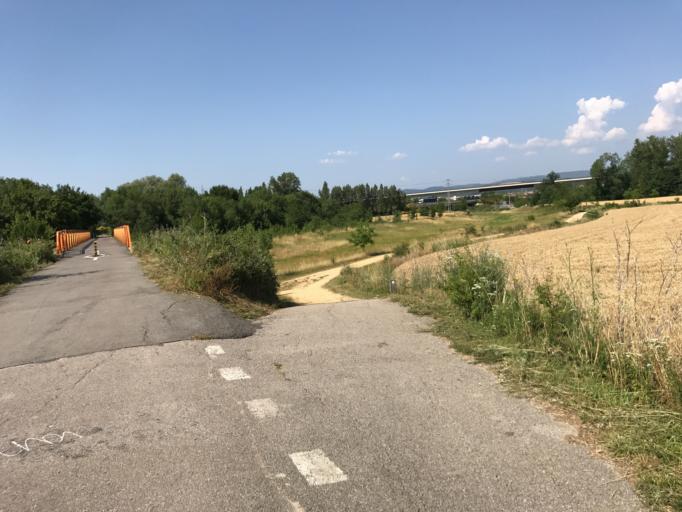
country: ES
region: Basque Country
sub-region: Provincia de Alava
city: Gasteiz / Vitoria
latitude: 42.8791
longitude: -2.6469
